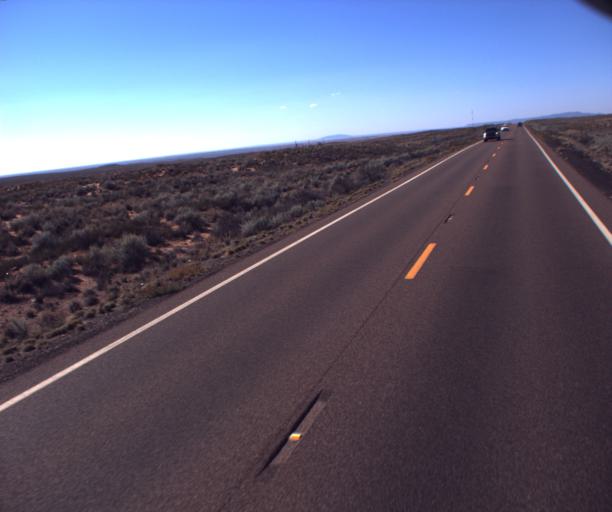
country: US
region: Arizona
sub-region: Navajo County
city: Winslow
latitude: 35.0443
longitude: -110.6051
